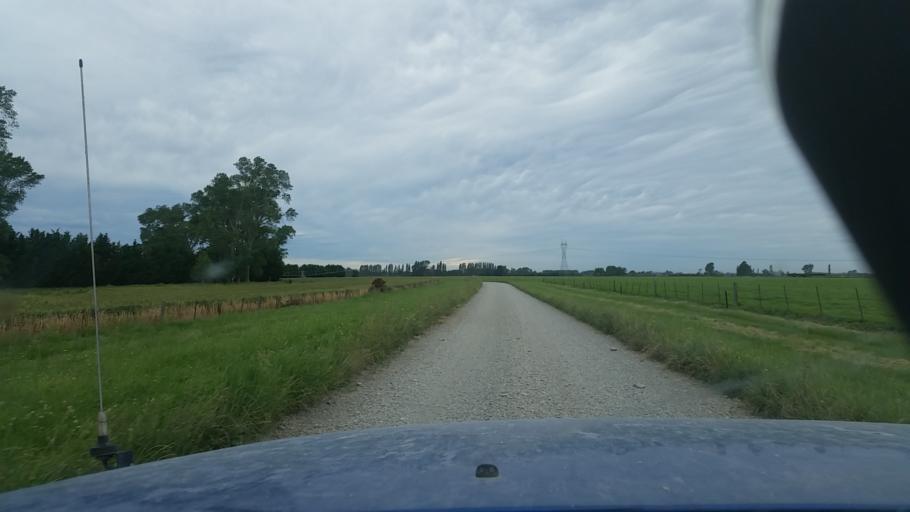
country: NZ
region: Canterbury
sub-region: Ashburton District
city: Ashburton
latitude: -43.8166
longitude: 171.6292
